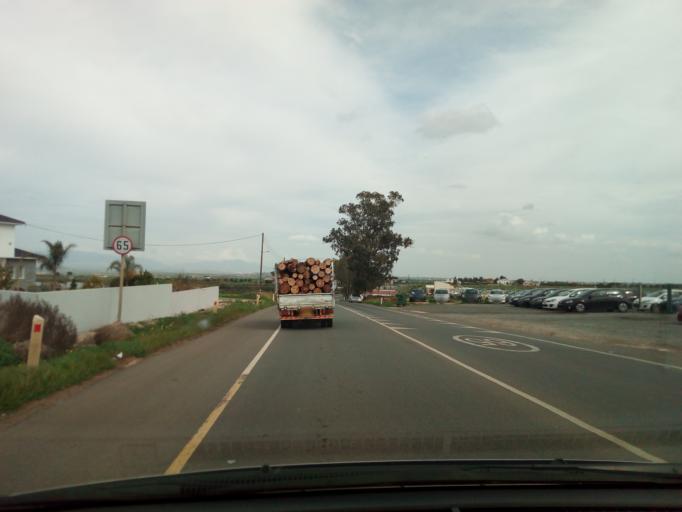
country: CY
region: Lefkosia
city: Peristerona
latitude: 35.1336
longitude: 33.0951
